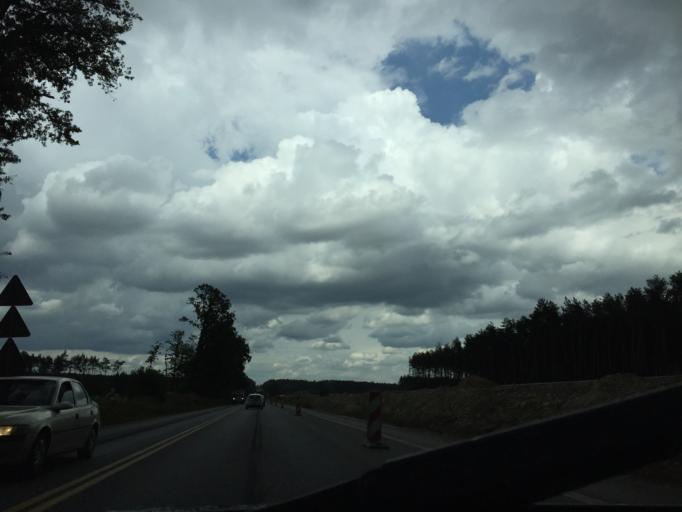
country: PL
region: Swietokrzyskie
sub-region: Powiat jedrzejowski
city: Jedrzejow
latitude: 50.6810
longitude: 20.3532
